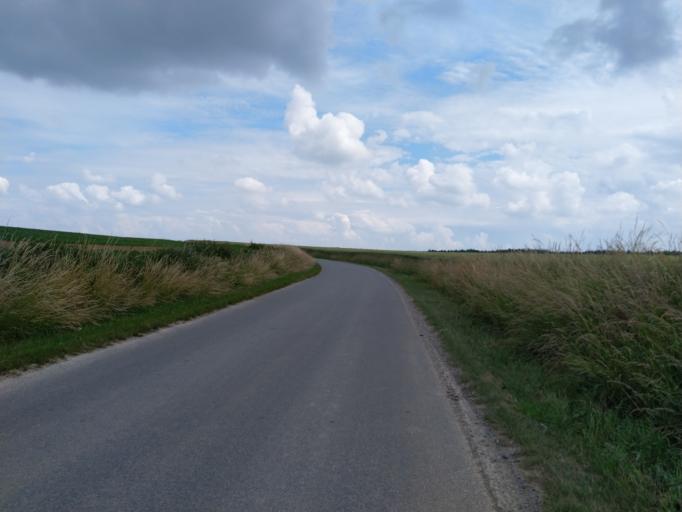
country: FR
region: Nord-Pas-de-Calais
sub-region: Departement du Nord
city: Boussois
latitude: 50.3490
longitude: 4.0232
